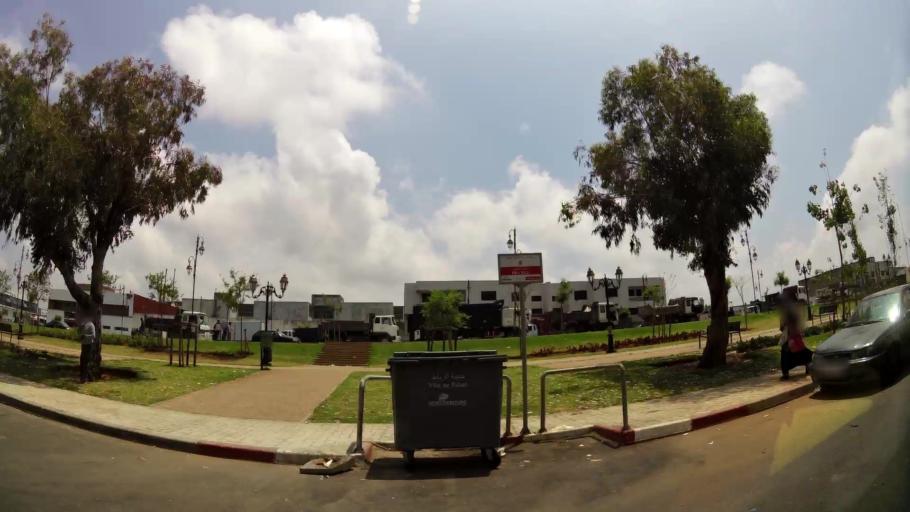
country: MA
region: Rabat-Sale-Zemmour-Zaer
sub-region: Rabat
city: Rabat
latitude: 33.9844
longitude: -6.8757
